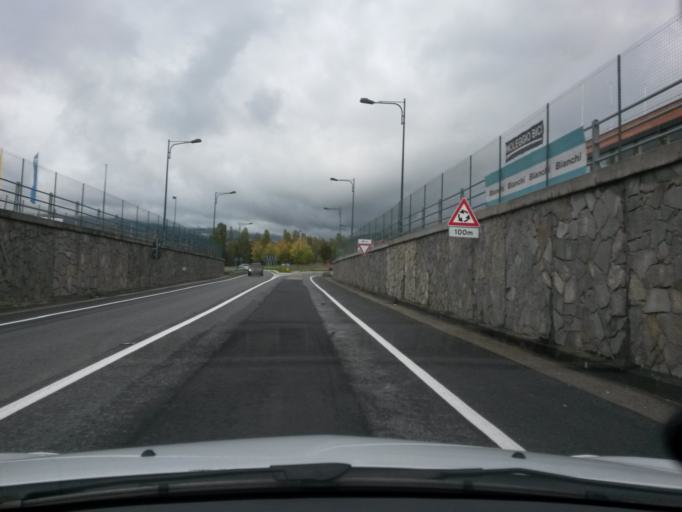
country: IT
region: Piedmont
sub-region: Provincia di Torino
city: Drubiaglio-Grangia
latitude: 45.0833
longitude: 7.4128
